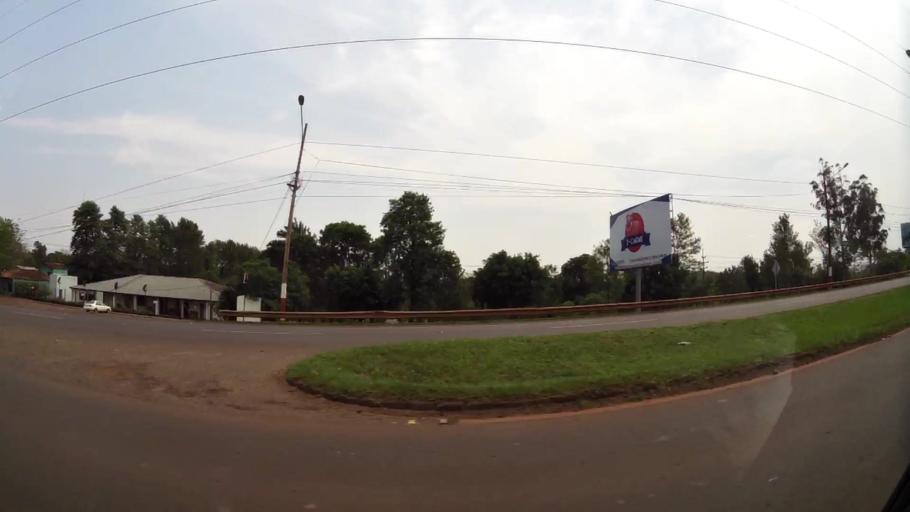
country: PY
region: Alto Parana
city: Ciudad del Este
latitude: -25.4851
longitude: -54.6278
